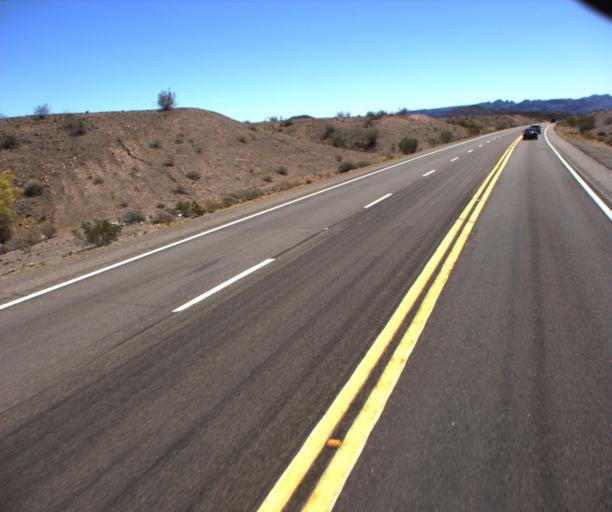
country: US
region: Arizona
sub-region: Mohave County
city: Lake Havasu City
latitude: 34.3903
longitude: -114.1693
